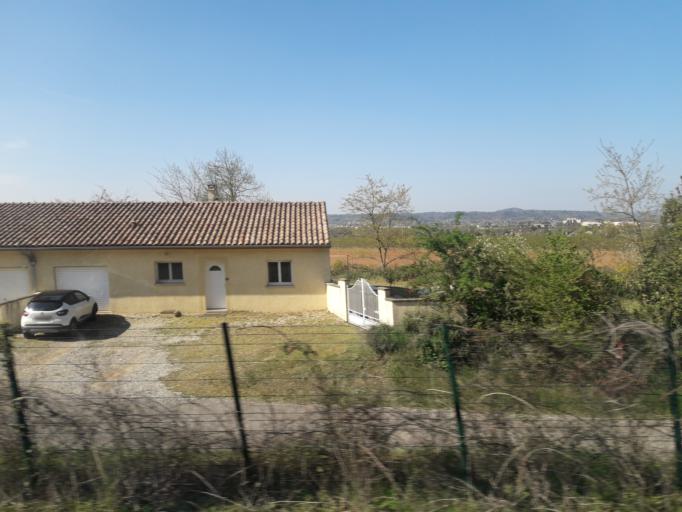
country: FR
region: Rhone-Alpes
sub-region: Departement de la Drome
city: Romans-sur-Isere
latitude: 45.0236
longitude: 5.0153
